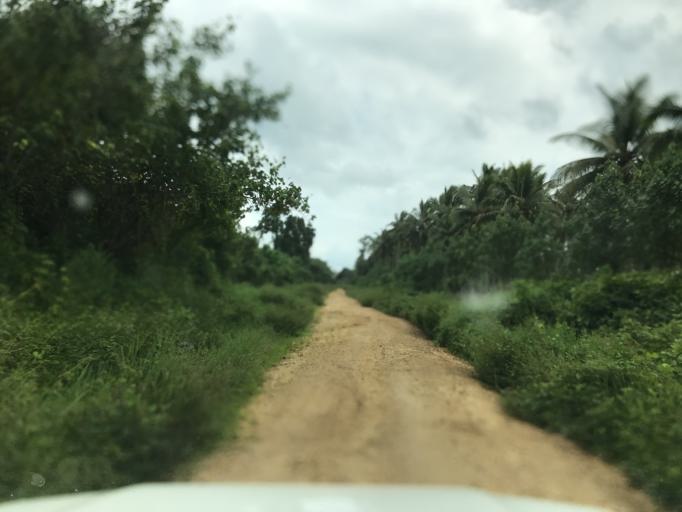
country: VU
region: Sanma
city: Port-Olry
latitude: -15.1858
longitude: 167.0255
